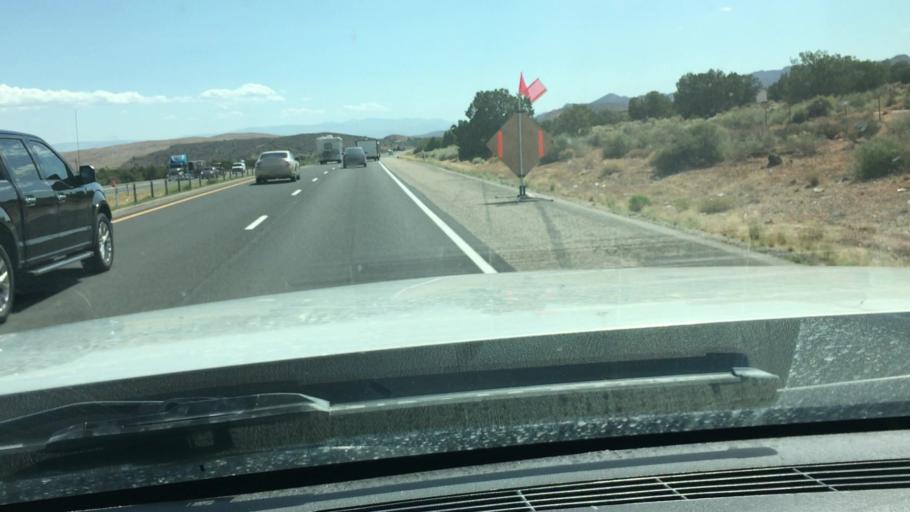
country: US
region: Utah
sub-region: Washington County
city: Toquerville
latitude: 37.2596
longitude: -113.3307
